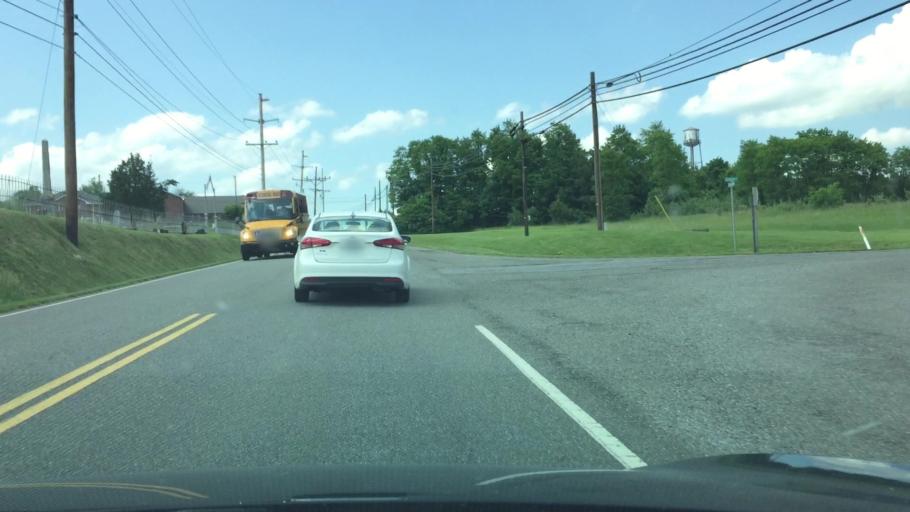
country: US
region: Virginia
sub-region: Pulaski County
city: Dublin
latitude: 37.0839
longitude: -80.6832
